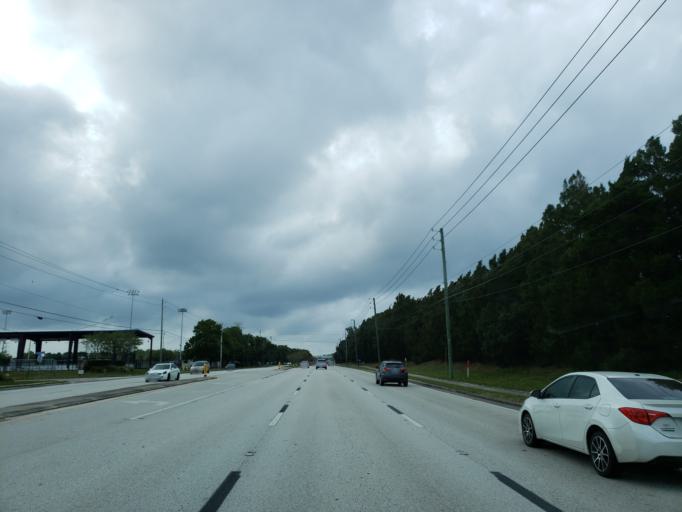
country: US
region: Florida
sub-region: Pinellas County
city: Saint George
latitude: 28.0558
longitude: -82.7034
